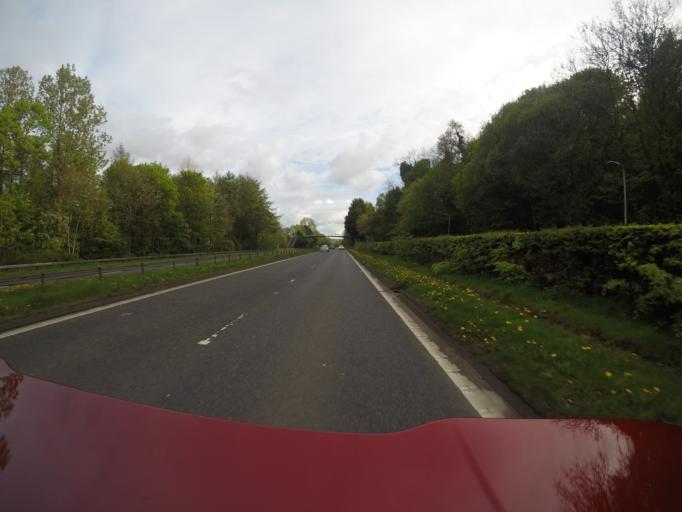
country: GB
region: Scotland
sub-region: West Dunbartonshire
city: Renton
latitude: 55.9705
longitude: -4.5877
